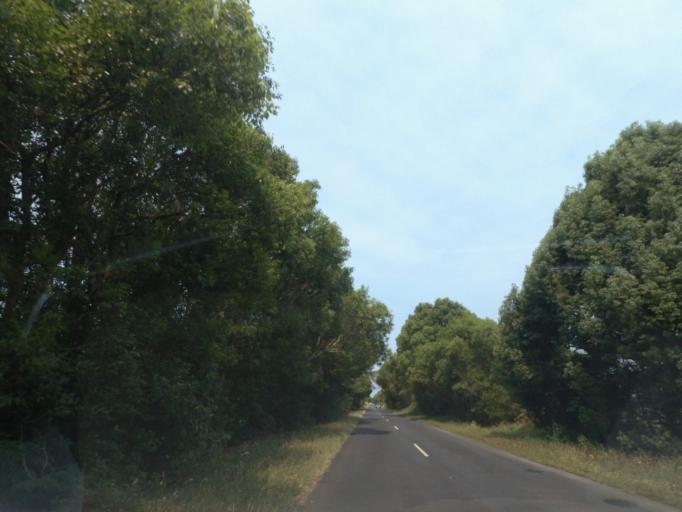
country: AU
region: New South Wales
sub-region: Tweed
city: Pottsville Beach
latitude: -28.4562
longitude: 153.5459
